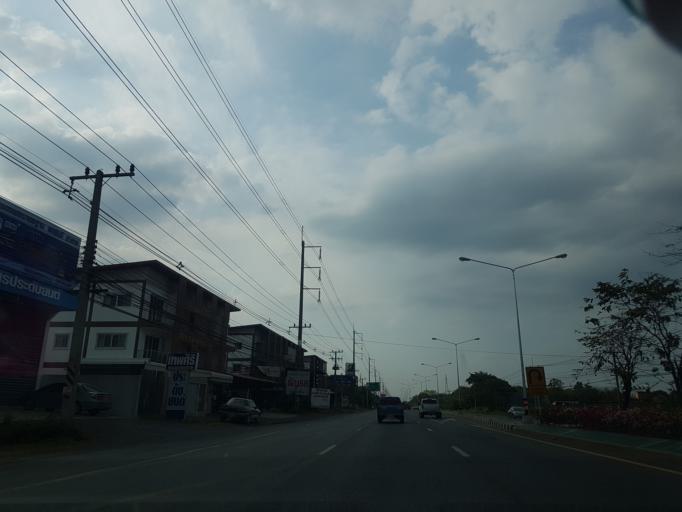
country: TH
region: Sara Buri
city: Phra Phutthabat
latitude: 14.7375
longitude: 100.7717
